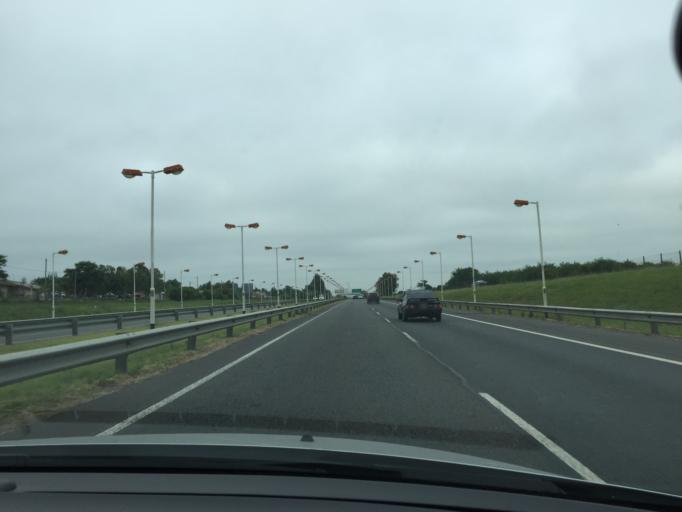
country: AR
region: Buenos Aires
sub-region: Partido de Ezeiza
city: Ezeiza
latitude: -34.8384
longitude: -58.5217
